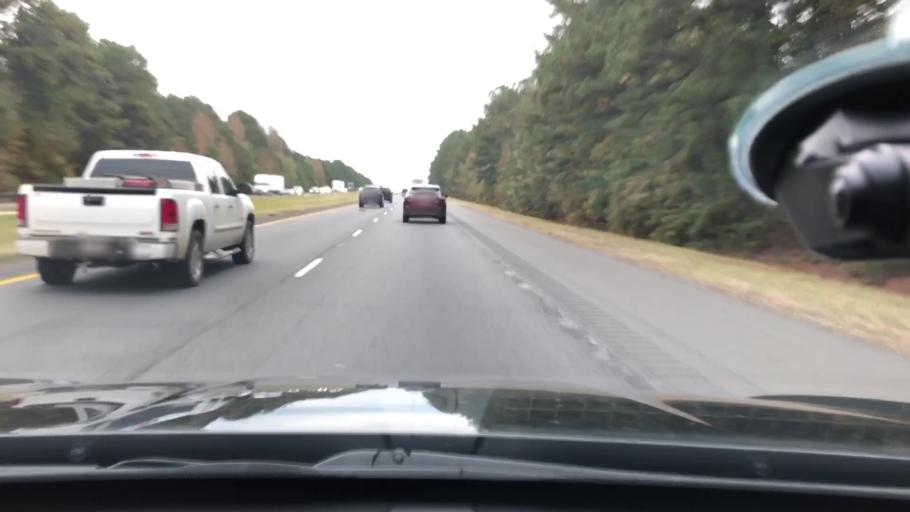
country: US
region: Arkansas
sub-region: Clark County
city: Arkadelphia
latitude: 34.0404
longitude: -93.1405
